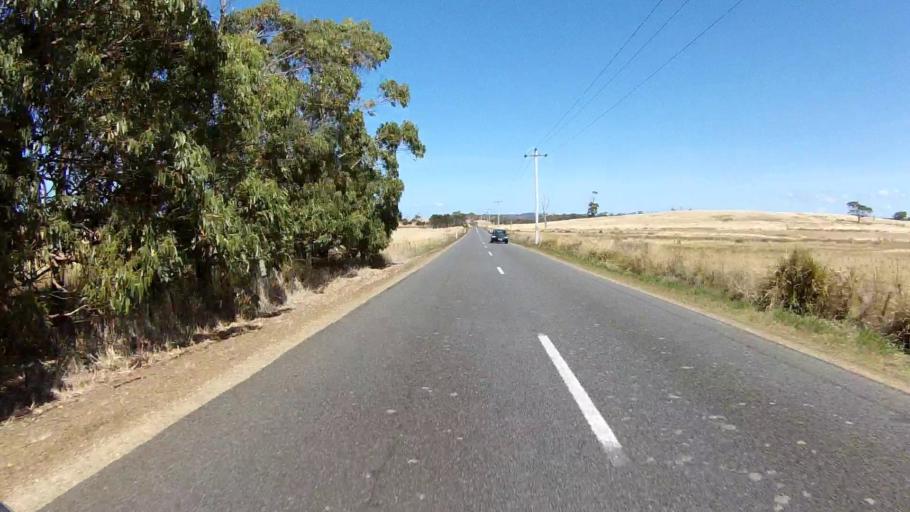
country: AU
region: Tasmania
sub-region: Sorell
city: Sorell
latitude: -42.2730
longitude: 148.0041
